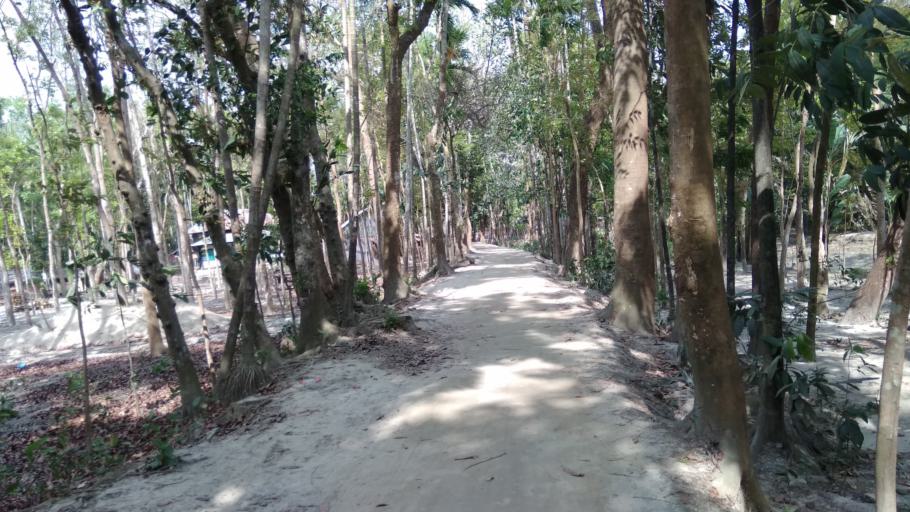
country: BD
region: Barisal
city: Gaurnadi
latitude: 22.9933
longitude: 90.3732
